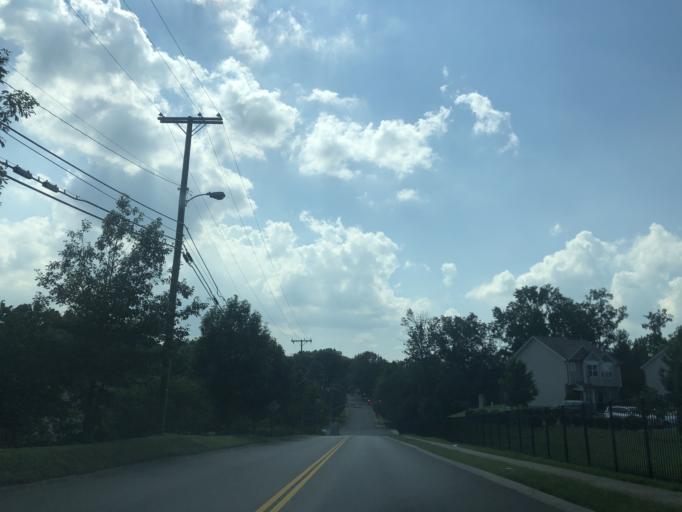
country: US
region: Tennessee
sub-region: Davidson County
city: Lakewood
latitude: 36.1454
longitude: -86.6245
